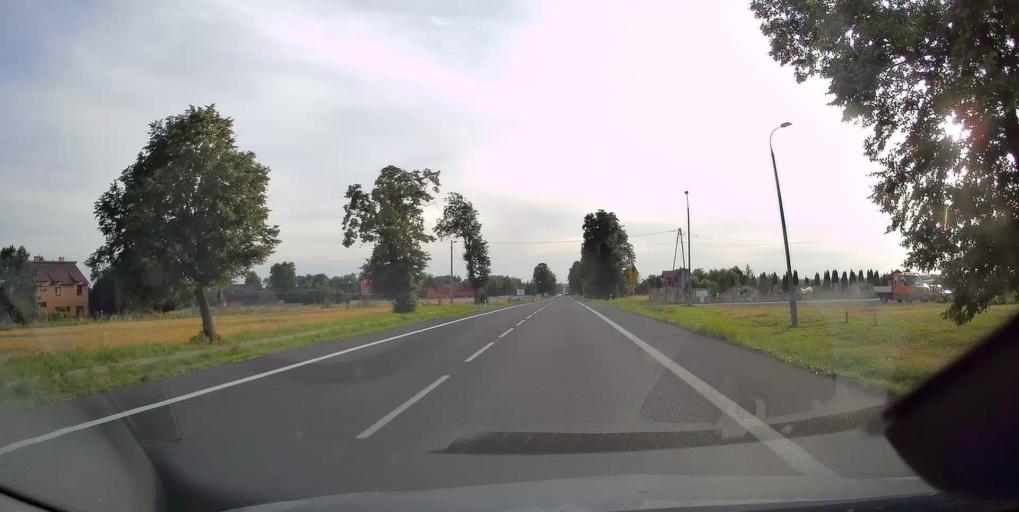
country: PL
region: Lesser Poland Voivodeship
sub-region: Powiat krakowski
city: Slomniki
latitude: 50.2316
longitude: 20.0652
